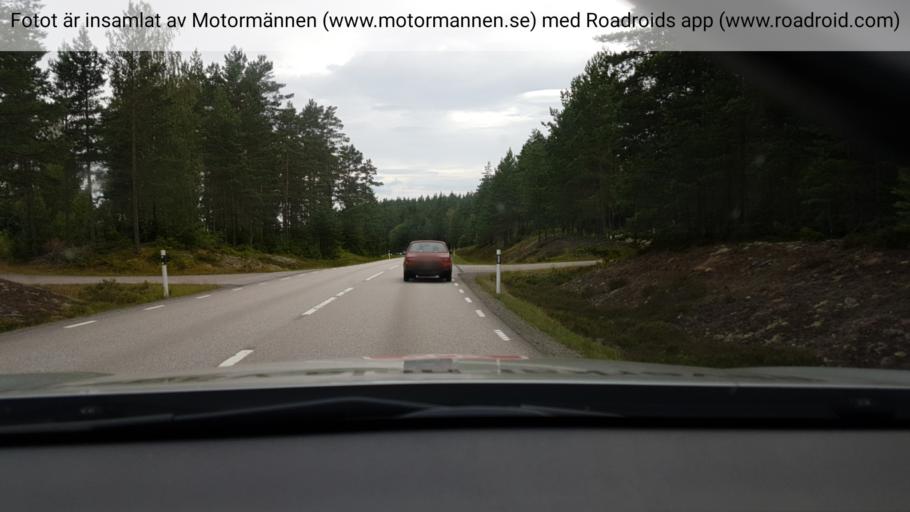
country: SE
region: Vaestra Goetaland
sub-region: Bengtsfors Kommun
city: Dals Langed
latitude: 58.8950
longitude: 12.2135
